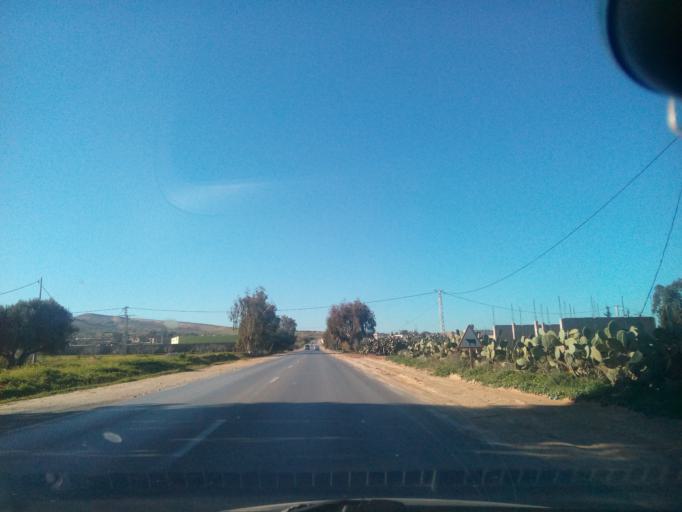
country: DZ
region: Relizane
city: Relizane
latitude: 35.9027
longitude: 0.5225
